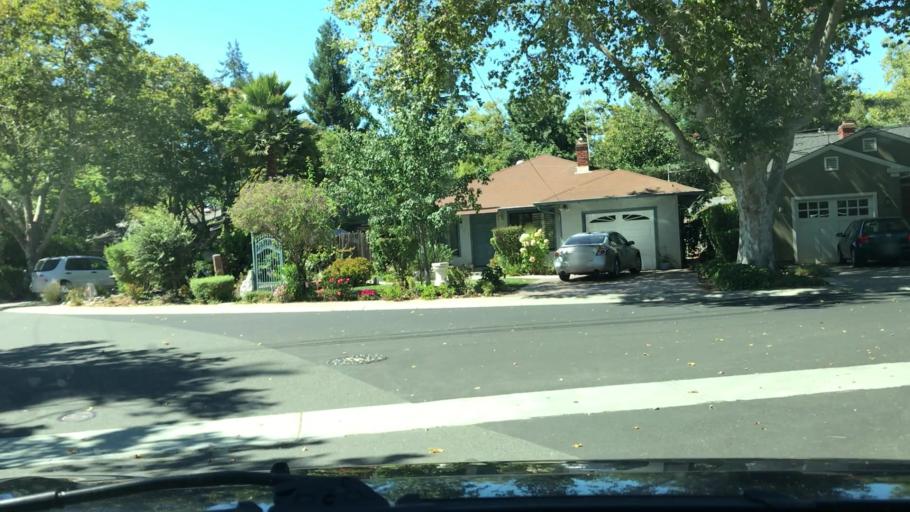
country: US
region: California
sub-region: San Mateo County
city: Menlo Park
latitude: 37.4554
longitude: -122.1612
